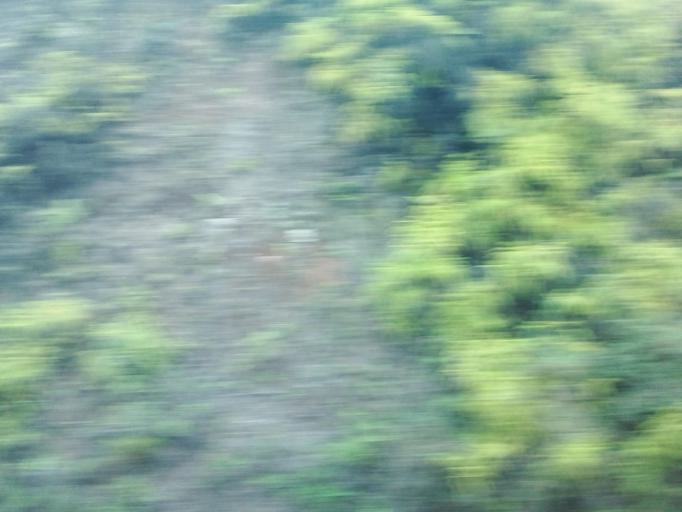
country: BR
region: Minas Gerais
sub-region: Rio Piracicaba
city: Rio Piracicaba
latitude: -19.8815
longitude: -43.1282
